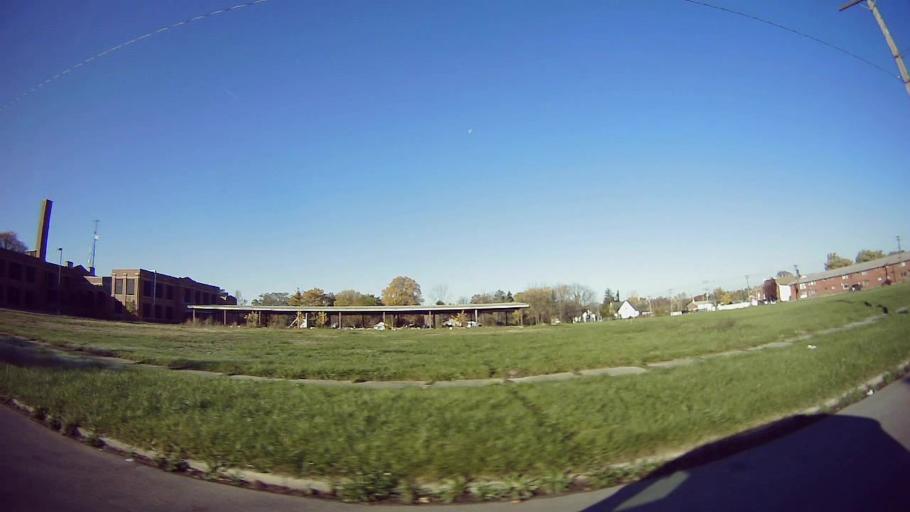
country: US
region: Michigan
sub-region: Wayne County
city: Dearborn
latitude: 42.3720
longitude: -83.1681
